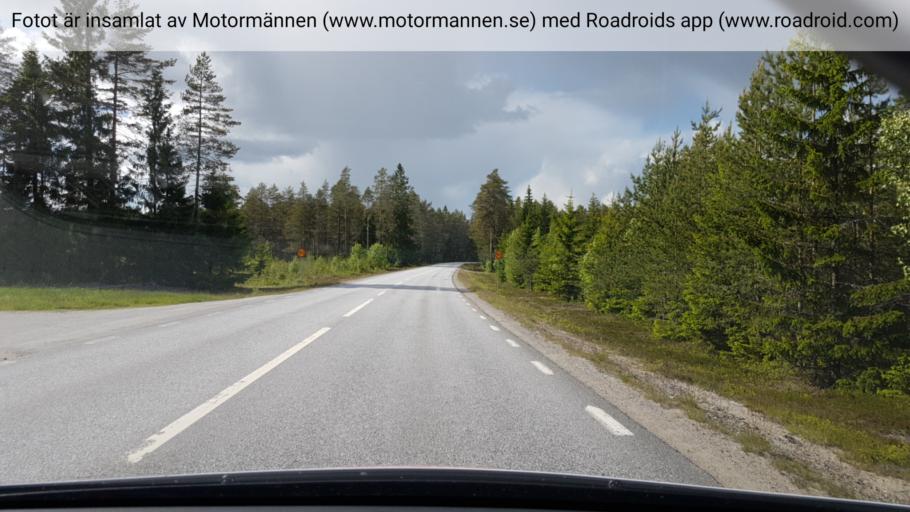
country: SE
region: Vaesterbotten
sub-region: Umea Kommun
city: Roback
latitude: 63.9451
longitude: 20.1473
